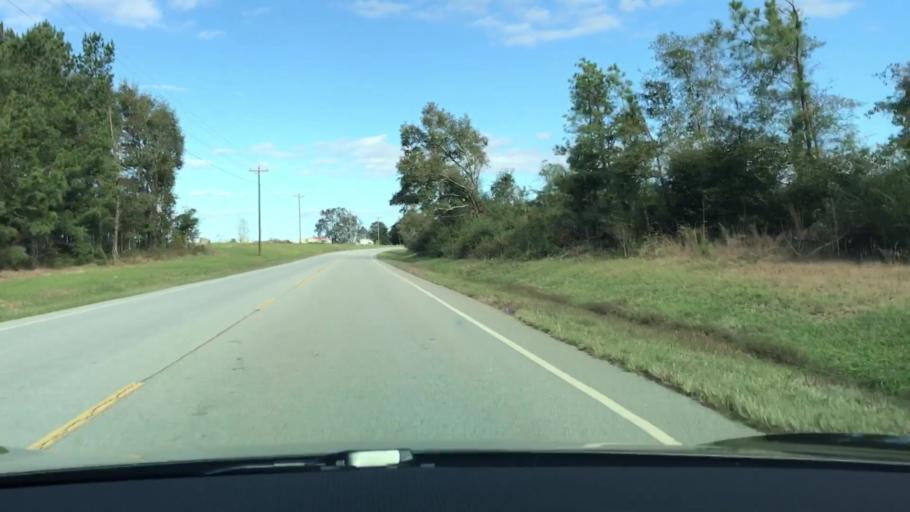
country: US
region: Georgia
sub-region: Jefferson County
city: Wrens
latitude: 33.1393
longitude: -82.4558
